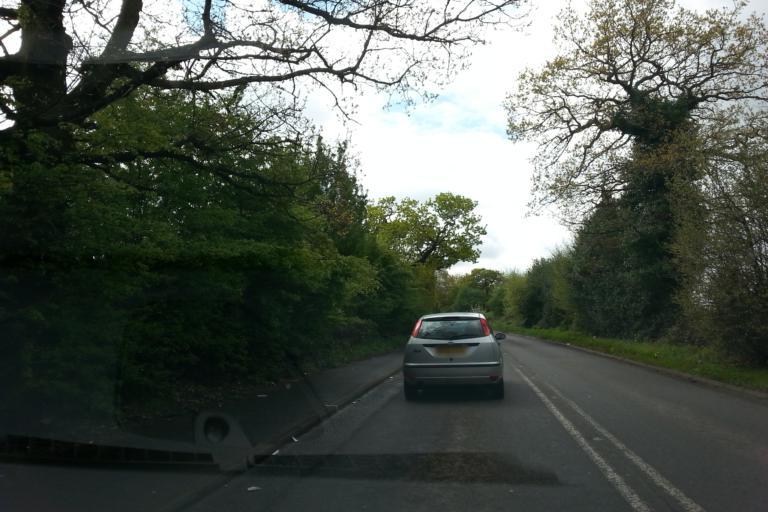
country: GB
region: England
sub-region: Staffordshire
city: Essington
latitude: 52.6262
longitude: -2.0465
